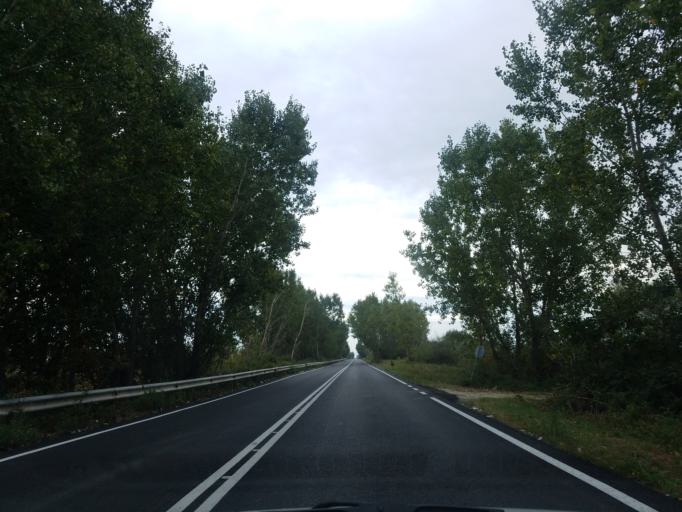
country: GR
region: Thessaly
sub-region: Nomos Kardhitsas
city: Agnantero
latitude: 39.4621
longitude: 21.8540
